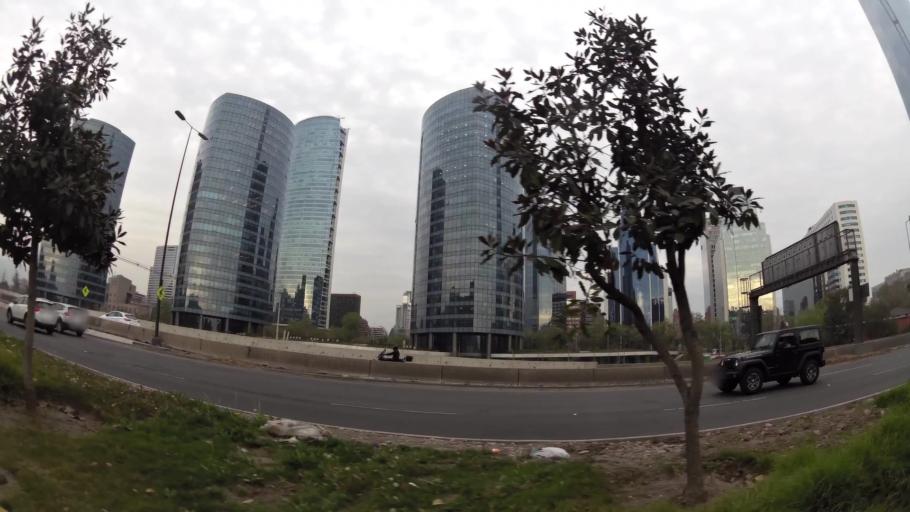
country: CL
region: Santiago Metropolitan
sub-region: Provincia de Santiago
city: Villa Presidente Frei, Nunoa, Santiago, Chile
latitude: -33.4140
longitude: -70.6075
